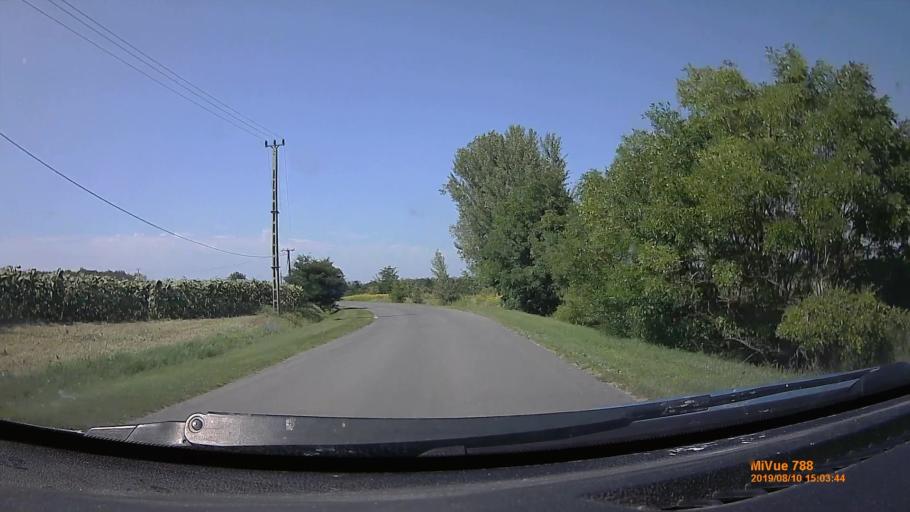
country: HU
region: Somogy
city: Lengyeltoti
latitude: 46.6691
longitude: 17.5714
